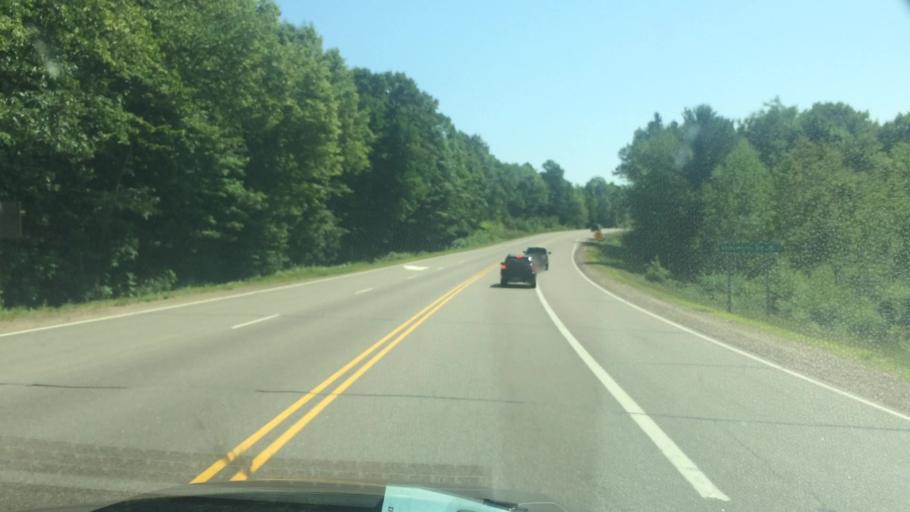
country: US
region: Wisconsin
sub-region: Oneida County
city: Rhinelander
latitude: 45.6174
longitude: -89.5242
